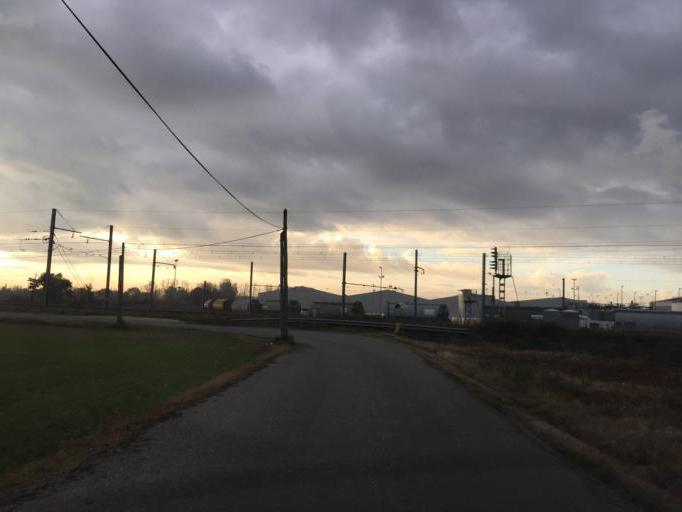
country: FR
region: Provence-Alpes-Cote d'Azur
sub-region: Departement du Vaucluse
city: Orange
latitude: 44.1321
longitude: 4.8472
